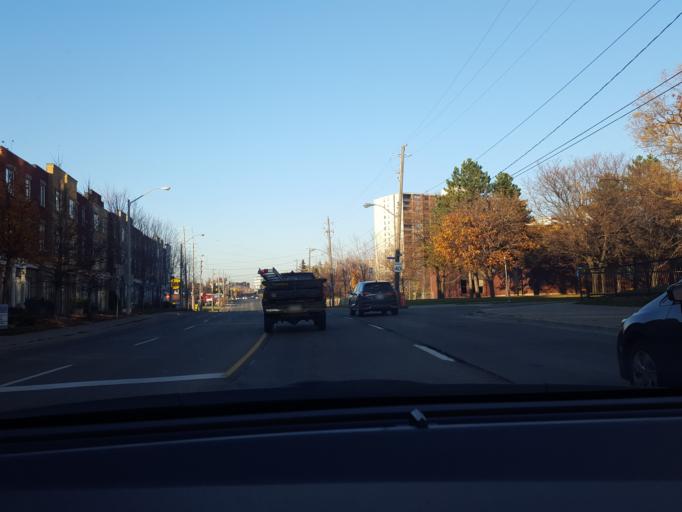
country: CA
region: Ontario
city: Scarborough
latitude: 43.7157
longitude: -79.3050
